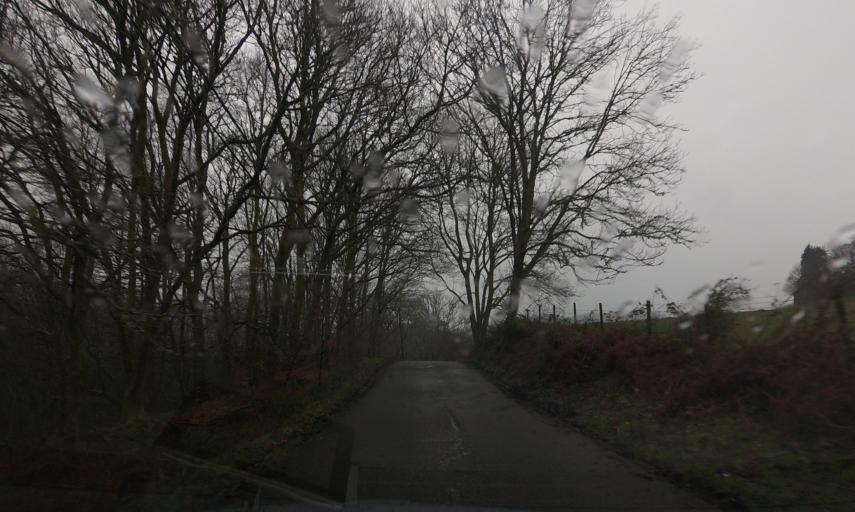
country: GB
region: Scotland
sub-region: West Dunbartonshire
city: Balloch
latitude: 56.1364
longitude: -4.6137
